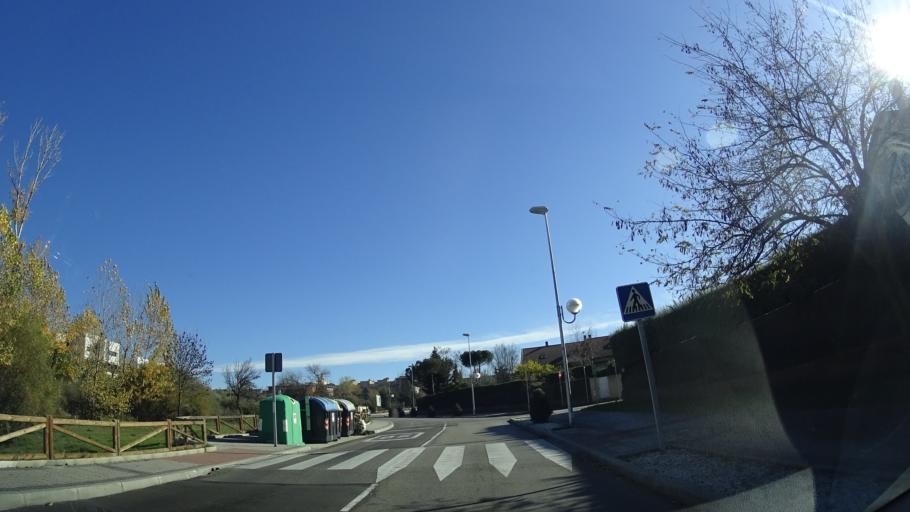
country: ES
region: Madrid
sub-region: Provincia de Madrid
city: Las Matas
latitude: 40.5204
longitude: -3.9077
